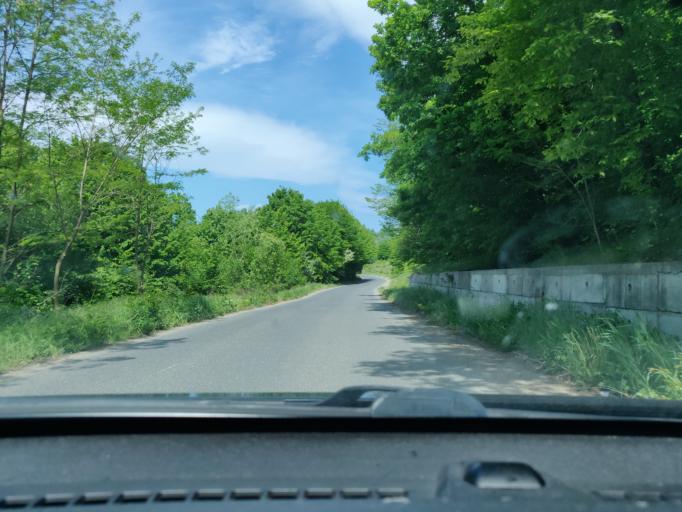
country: RO
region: Vrancea
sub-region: Comuna Vidra
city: Vidra
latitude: 45.9304
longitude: 26.8930
